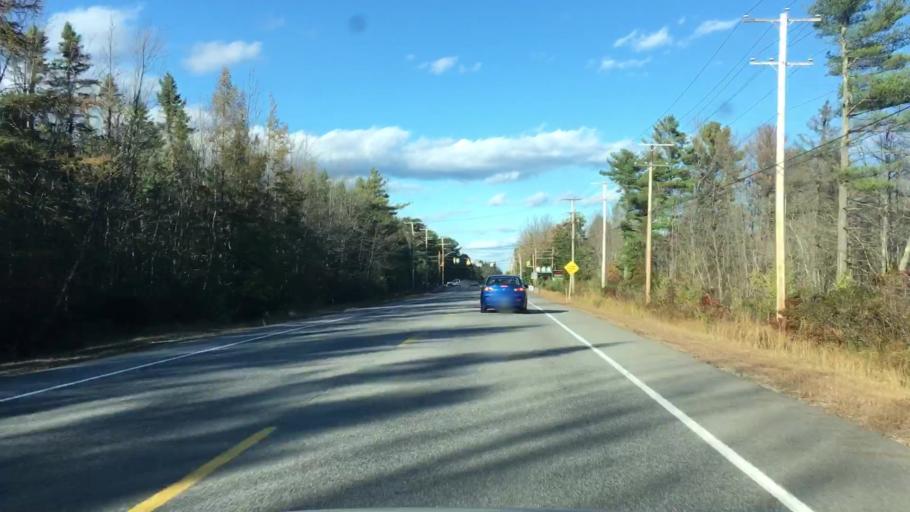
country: US
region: Maine
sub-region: Cumberland County
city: West Scarborough
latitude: 43.6069
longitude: -70.3630
